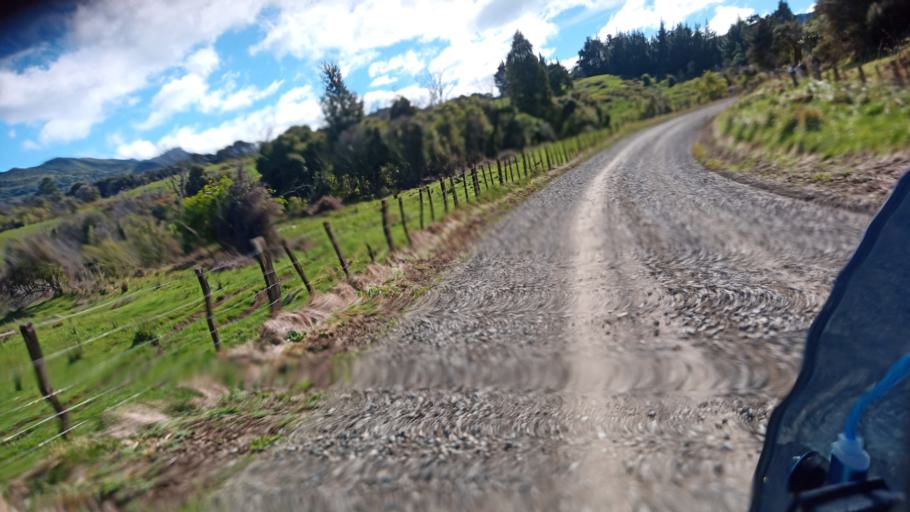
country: NZ
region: Hawke's Bay
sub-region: Wairoa District
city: Wairoa
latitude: -38.8180
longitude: 177.1570
